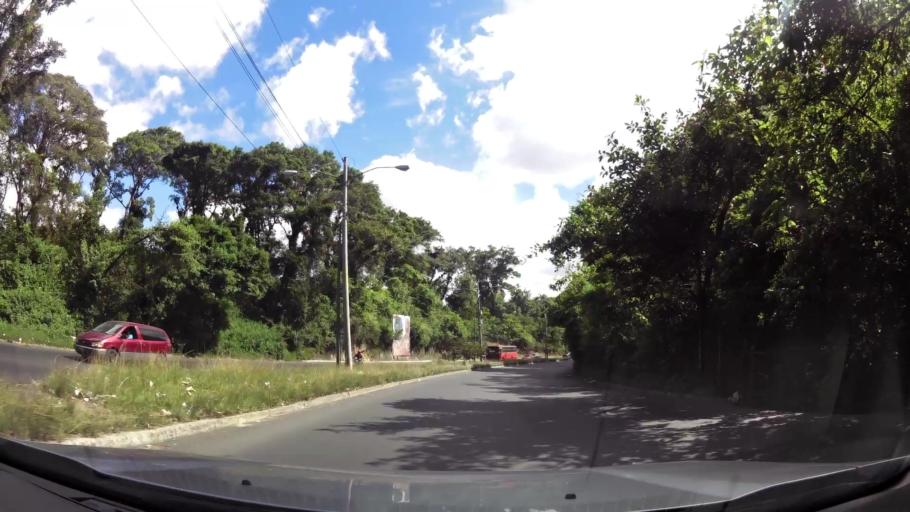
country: GT
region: Guatemala
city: Guatemala City
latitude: 14.6554
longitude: -90.5488
